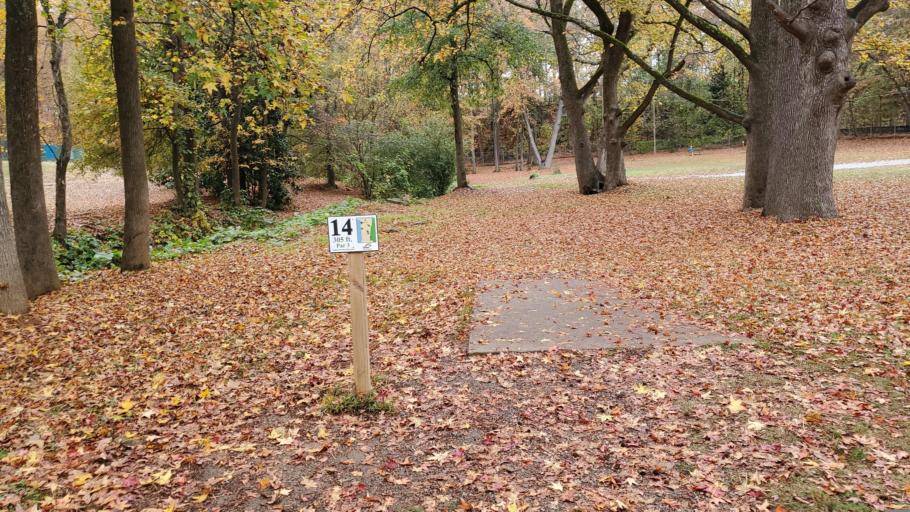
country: US
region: South Carolina
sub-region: Greenville County
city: Greer
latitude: 34.9307
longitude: -82.2387
